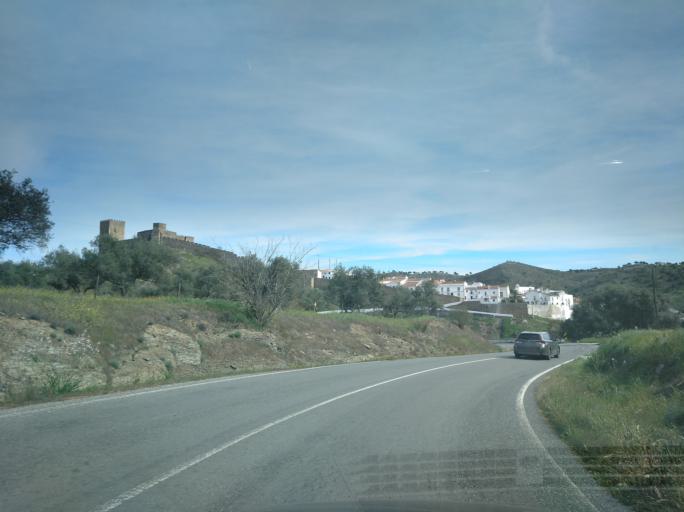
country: PT
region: Beja
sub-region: Mertola
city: Mertola
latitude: 37.6369
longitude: -7.6686
